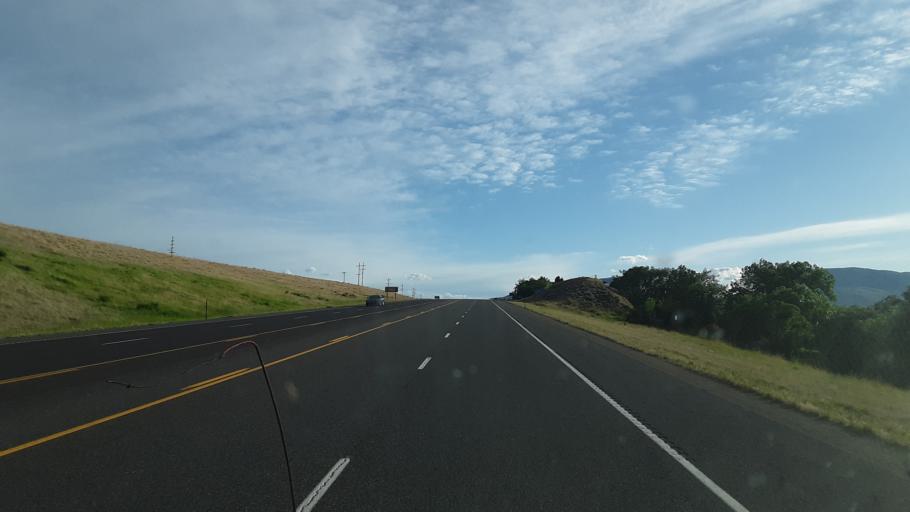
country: US
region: Wyoming
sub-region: Park County
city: Cody
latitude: 44.5396
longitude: -108.9980
